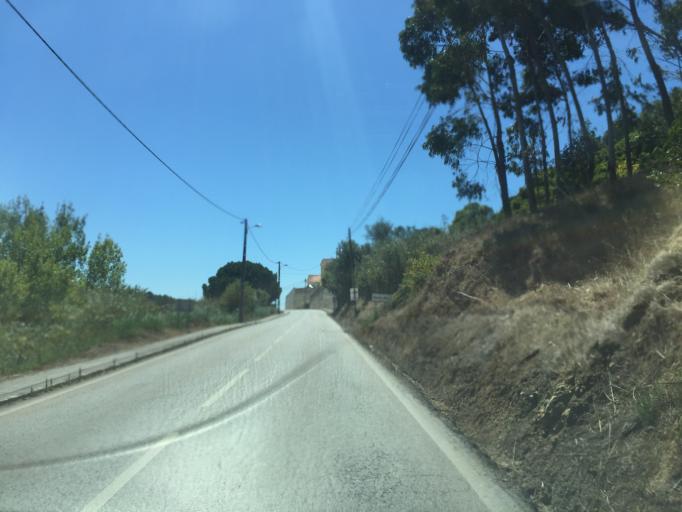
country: PT
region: Lisbon
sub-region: Torres Vedras
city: A dos Cunhados
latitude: 39.1810
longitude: -9.3233
